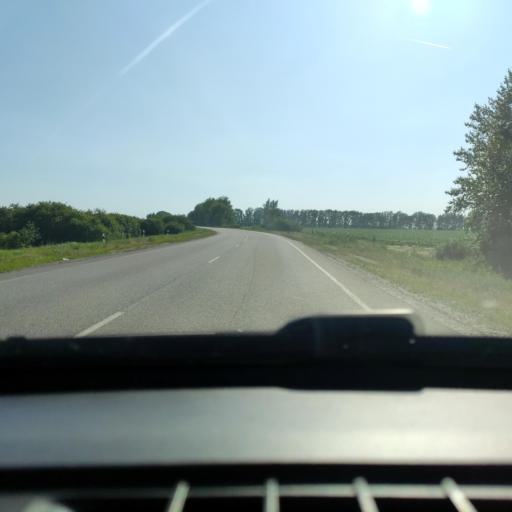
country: RU
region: Voronezj
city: Panino
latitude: 51.6273
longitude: 40.0435
